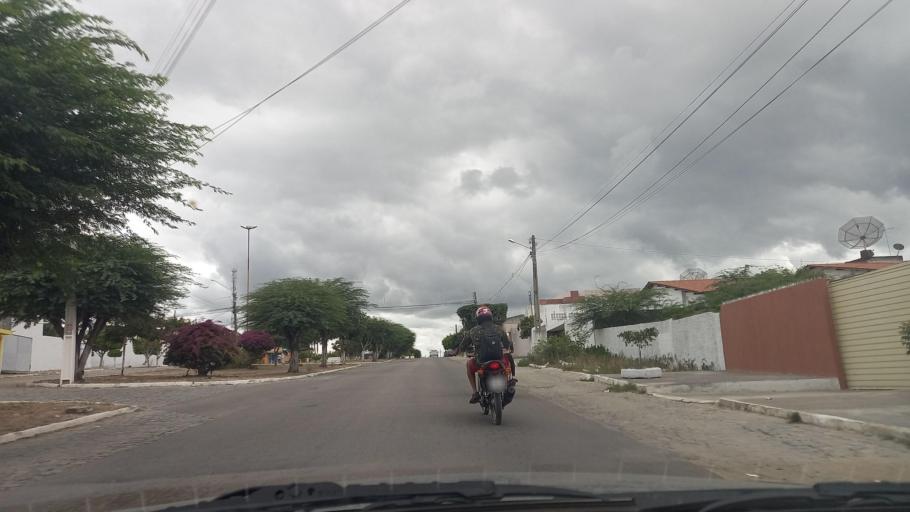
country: BR
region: Pernambuco
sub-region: Caruaru
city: Caruaru
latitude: -8.3262
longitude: -36.1399
